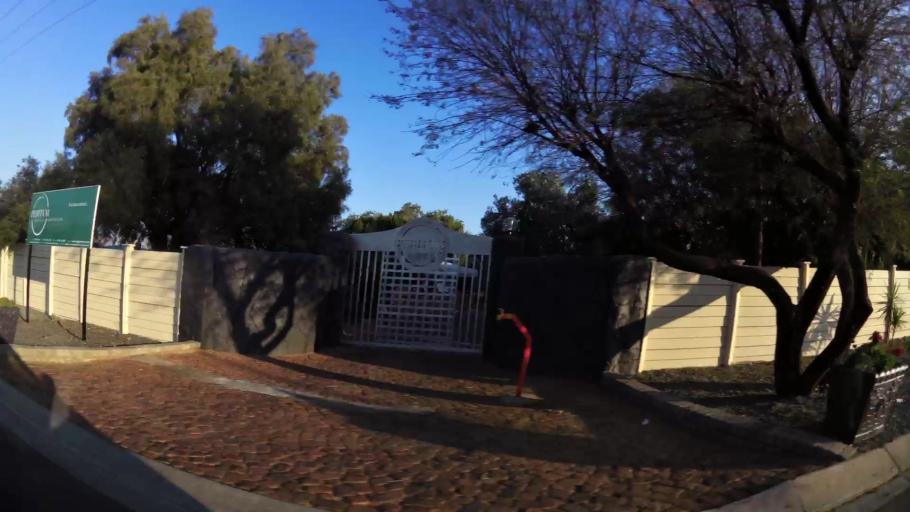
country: ZA
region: Orange Free State
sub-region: Mangaung Metropolitan Municipality
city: Bloemfontein
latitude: -29.0816
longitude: 26.1475
